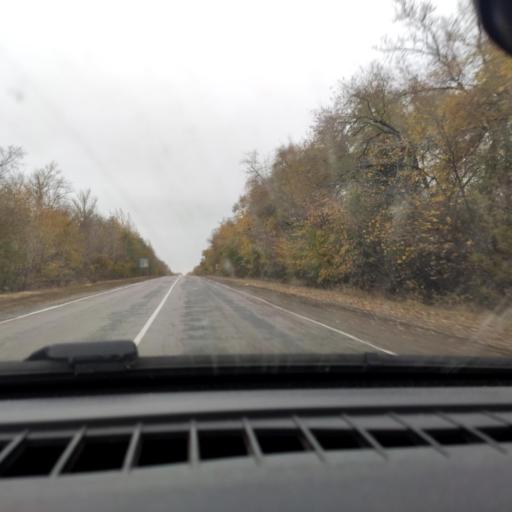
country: RU
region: Voronezj
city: Uryv-Pokrovka
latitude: 51.1442
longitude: 39.0573
